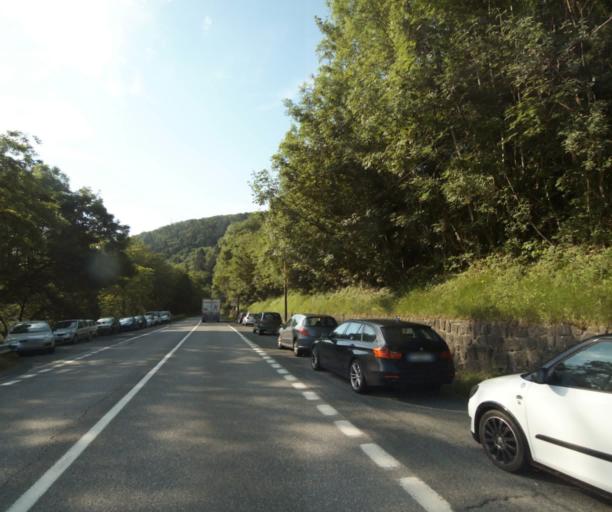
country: FR
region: Rhone-Alpes
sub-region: Departement de la Haute-Savoie
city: Thonon-les-Bains
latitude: 46.3671
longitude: 6.5038
